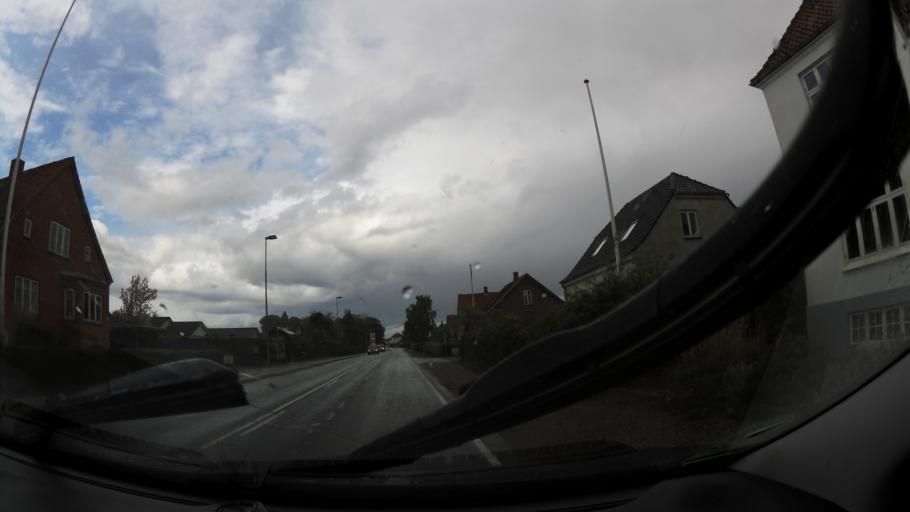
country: DK
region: South Denmark
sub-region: Nyborg Kommune
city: Nyborg
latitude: 55.3019
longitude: 10.7812
